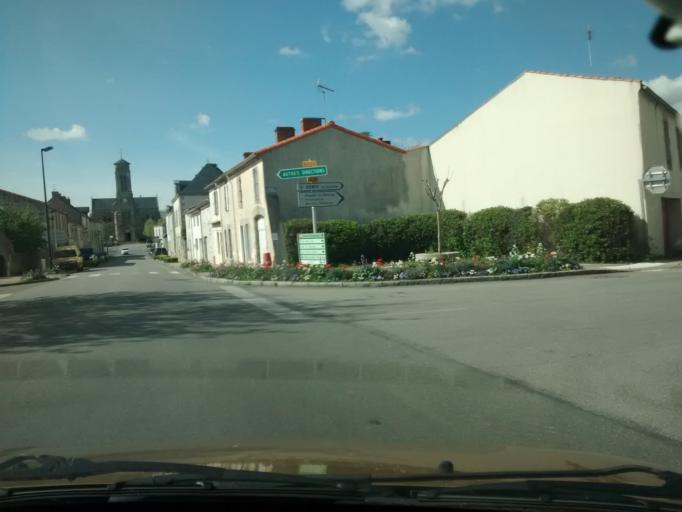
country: FR
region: Pays de la Loire
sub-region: Departement de la Vendee
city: Les Lucs-sur-Boulogne
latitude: 46.8415
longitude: -1.4925
